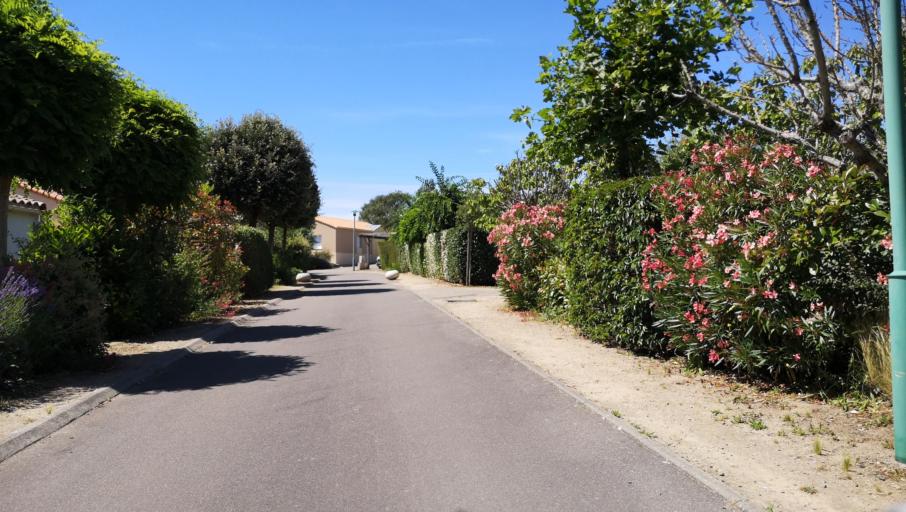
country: FR
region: Pays de la Loire
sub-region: Departement de la Vendee
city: Chateau-d'Olonne
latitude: 46.4782
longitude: -1.7329
